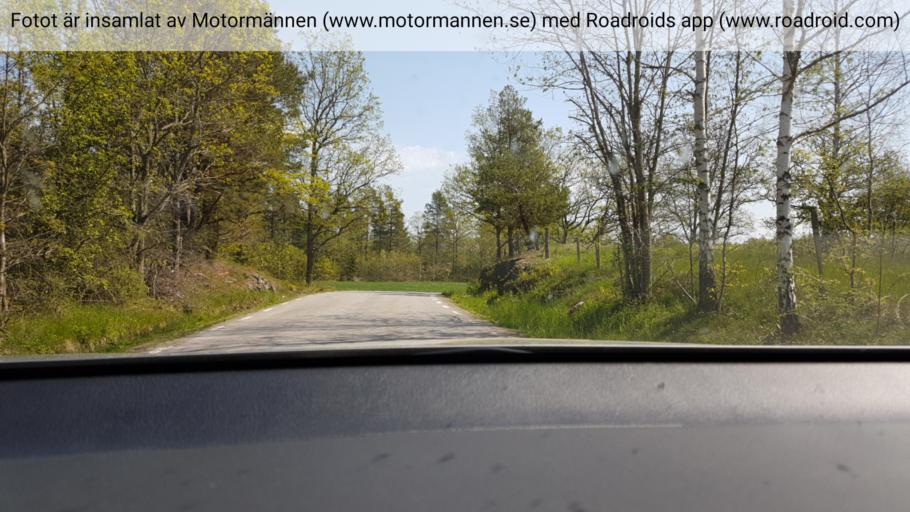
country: SE
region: Kalmar
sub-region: Vasterviks Kommun
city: Gamleby
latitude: 57.8952
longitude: 16.4373
